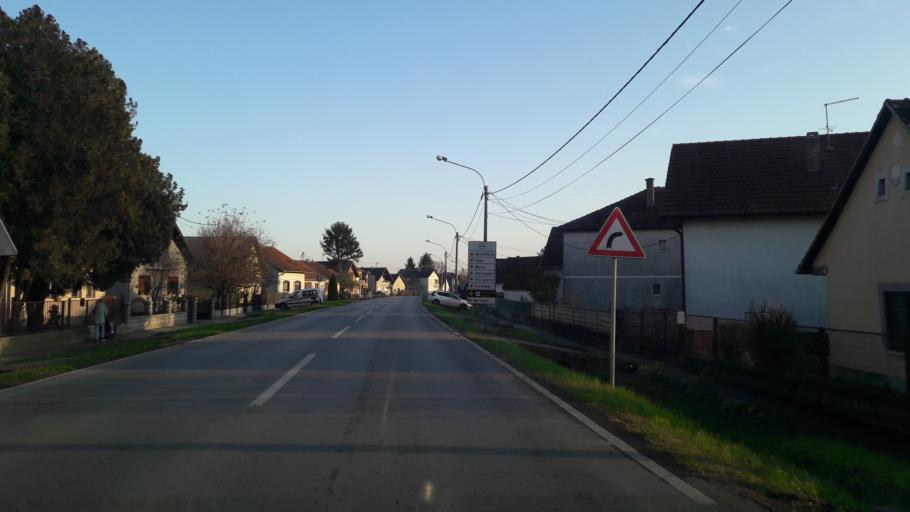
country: HR
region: Osjecko-Baranjska
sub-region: Grad Osijek
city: Bilje
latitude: 45.6091
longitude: 18.7402
